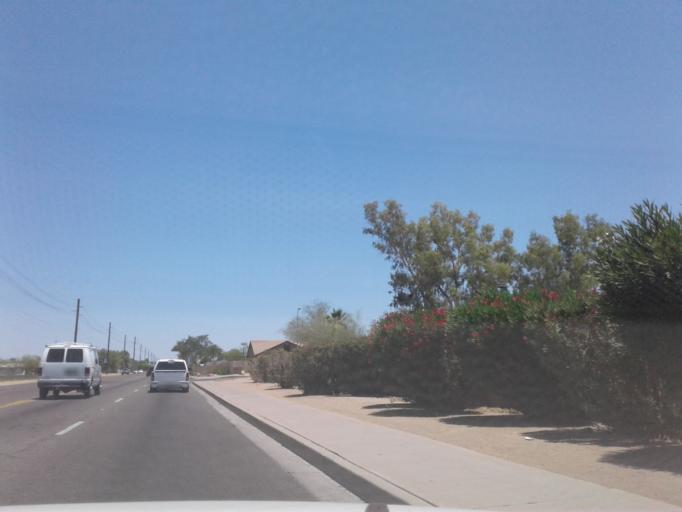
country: US
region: Arizona
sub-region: Maricopa County
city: Tolleson
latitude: 33.5087
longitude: -112.2514
